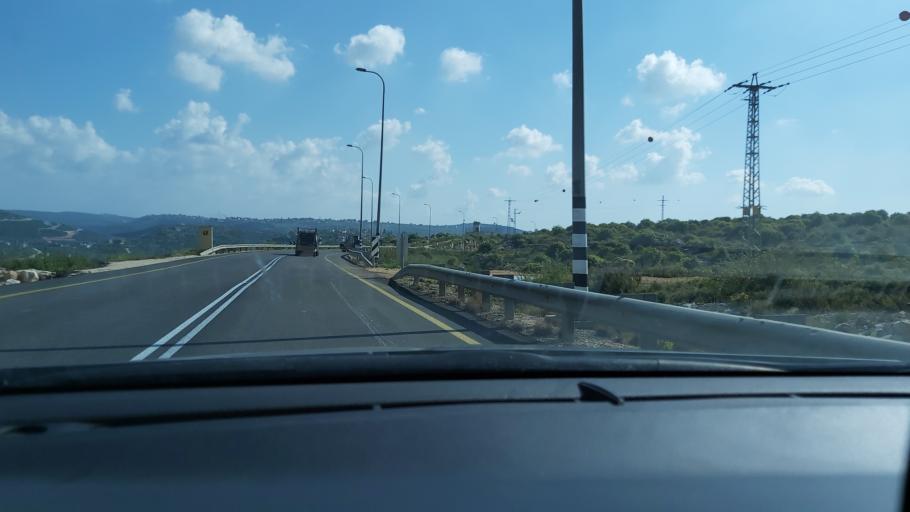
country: PS
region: West Bank
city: Bruqin
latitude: 32.0832
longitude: 35.1034
